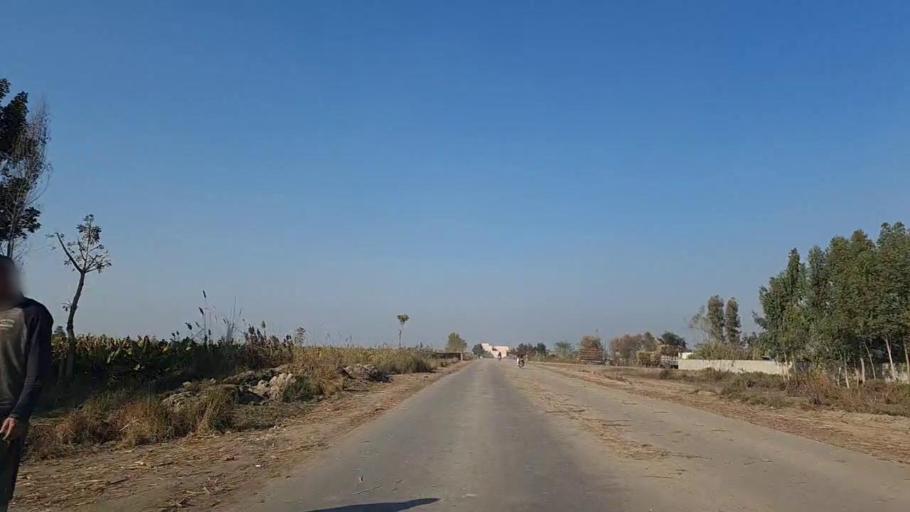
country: PK
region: Sindh
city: Bandhi
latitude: 26.6093
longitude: 68.3159
